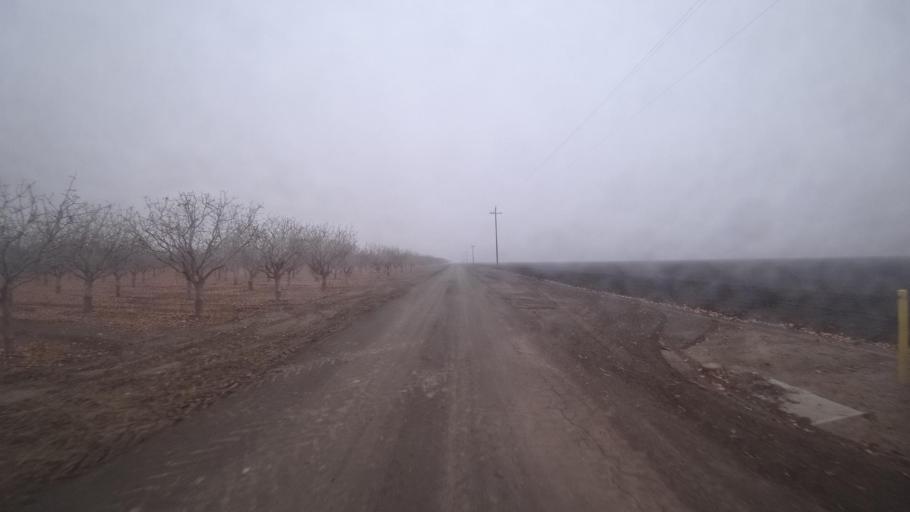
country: US
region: California
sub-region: Kern County
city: Buttonwillow
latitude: 35.4268
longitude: -119.5497
